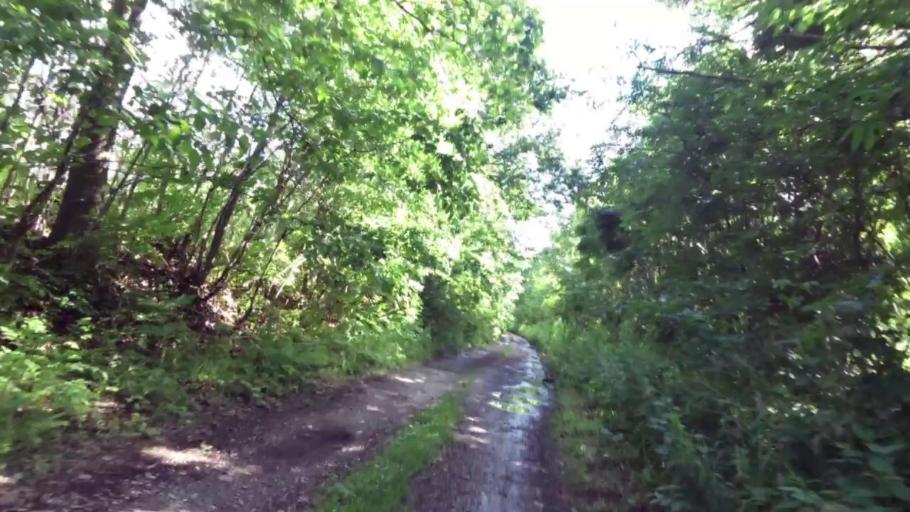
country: PL
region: West Pomeranian Voivodeship
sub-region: Powiat slawienski
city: Slawno
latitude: 54.5071
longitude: 16.7043
